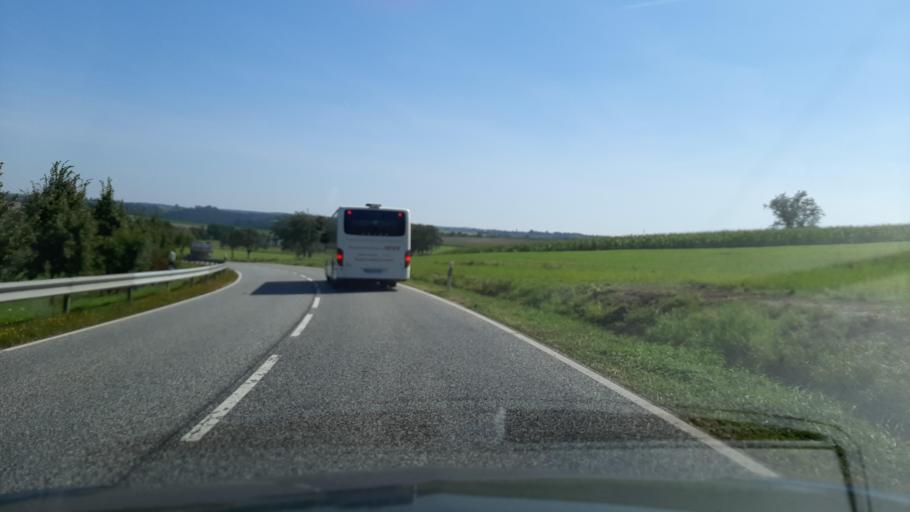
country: DE
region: Rheinland-Pfalz
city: Dudeldorf
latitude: 49.9710
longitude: 6.6296
